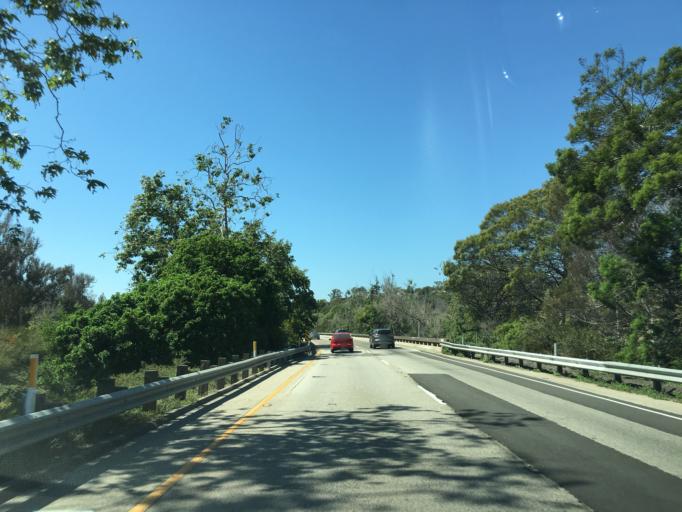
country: US
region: California
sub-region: Santa Barbara County
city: Montecito
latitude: 34.4225
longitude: -119.6535
